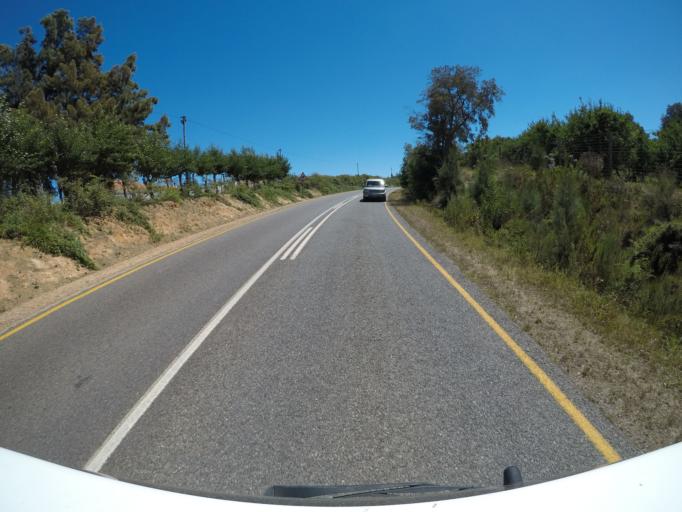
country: ZA
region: Western Cape
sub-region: Overberg District Municipality
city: Grabouw
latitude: -34.2132
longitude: 19.0520
